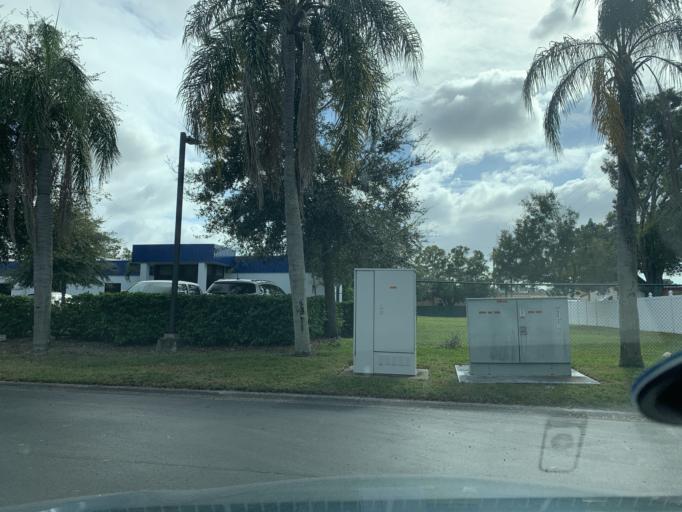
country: US
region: Florida
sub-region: Pinellas County
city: Ridgecrest
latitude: 27.8825
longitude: -82.7881
